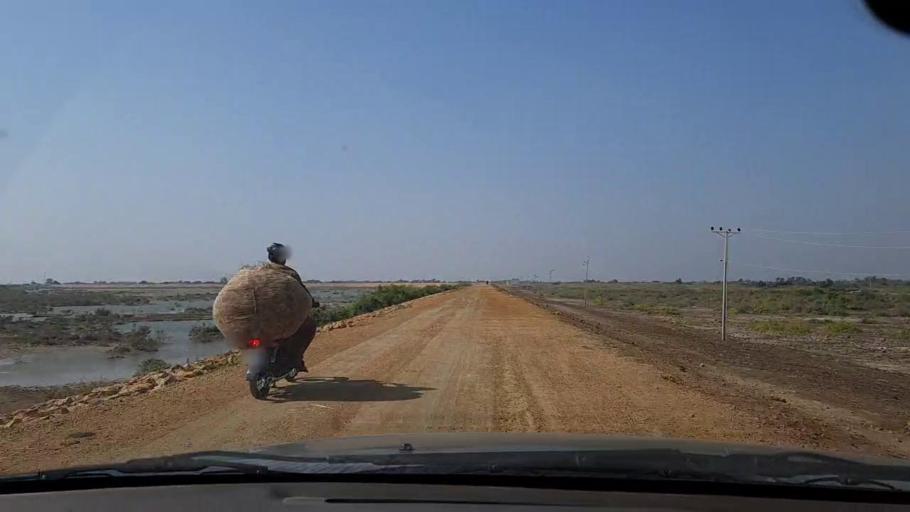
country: PK
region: Sindh
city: Chuhar Jamali
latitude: 24.4561
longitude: 67.8722
